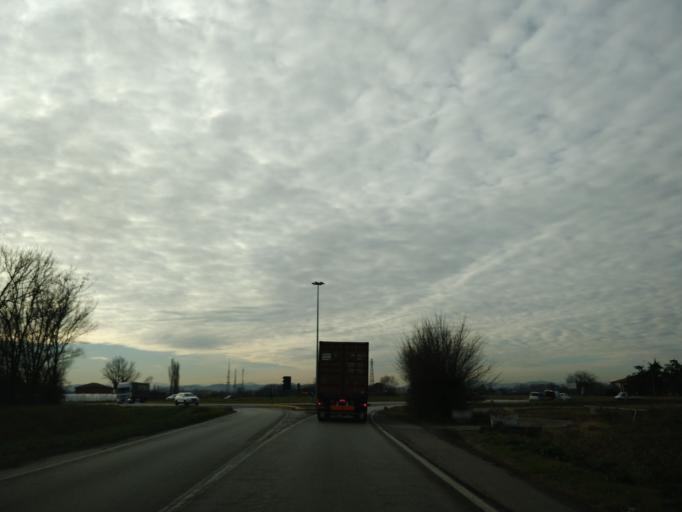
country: IT
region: Emilia-Romagna
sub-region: Provincia di Bologna
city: Progresso
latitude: 44.5722
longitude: 11.3818
